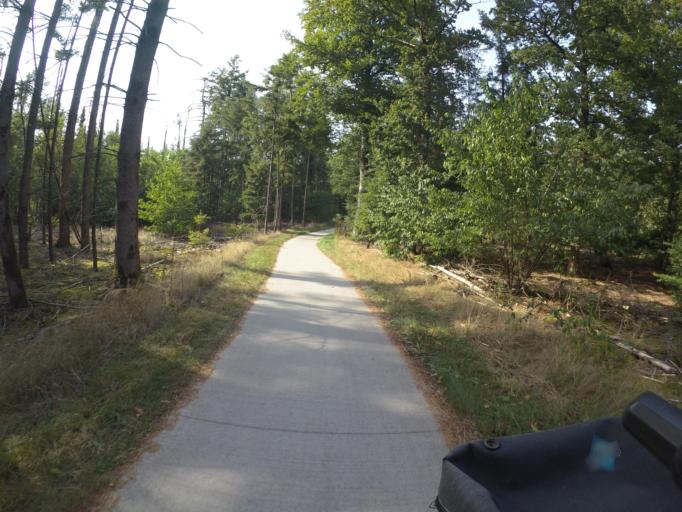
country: NL
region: Drenthe
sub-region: Gemeente Westerveld
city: Dwingeloo
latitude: 52.9156
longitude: 6.3382
